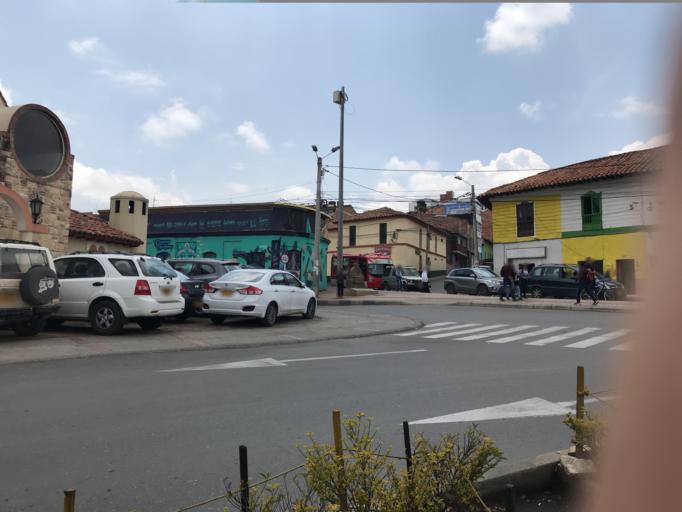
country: CO
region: Boyaca
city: Tunja
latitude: 5.5377
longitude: -73.3603
